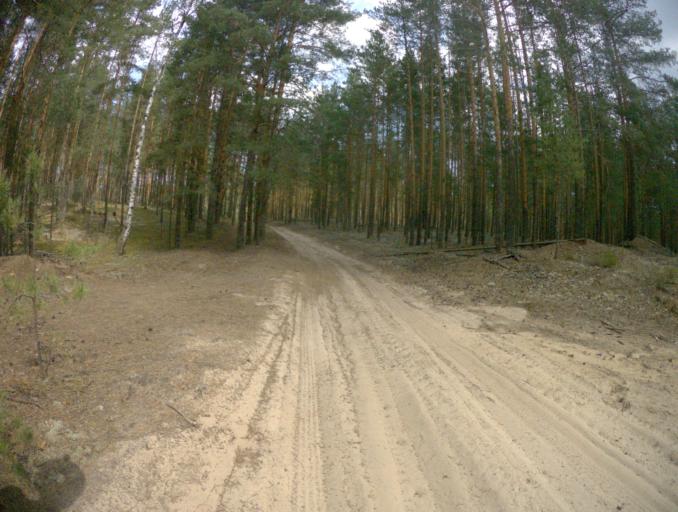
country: RU
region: Ivanovo
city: Talitsy
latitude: 56.3893
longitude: 42.3464
